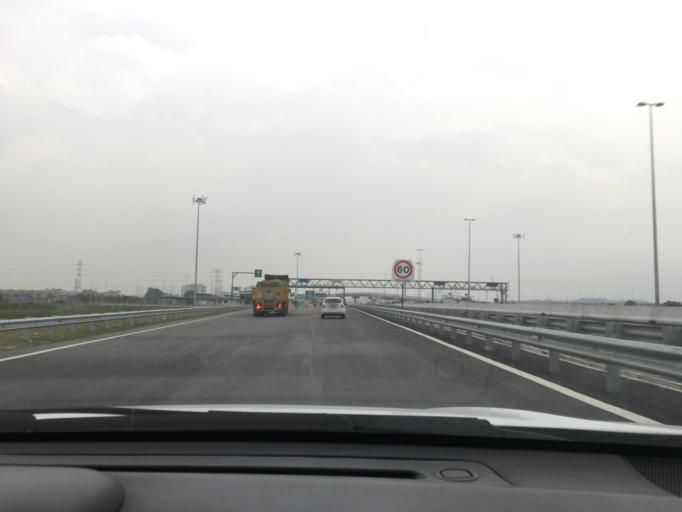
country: MY
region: Selangor
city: Klang
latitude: 3.0949
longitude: 101.4359
